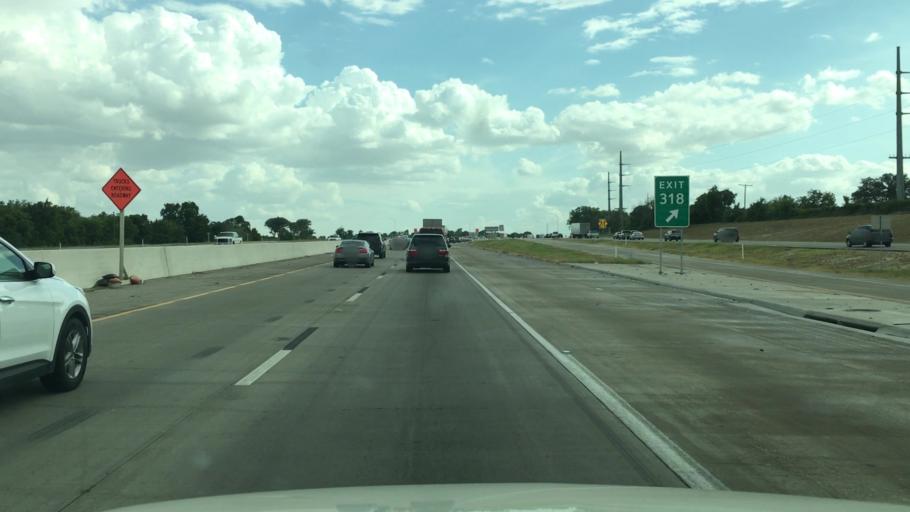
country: US
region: Texas
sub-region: McLennan County
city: Bruceville-Eddy
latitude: 31.3310
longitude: -97.2263
